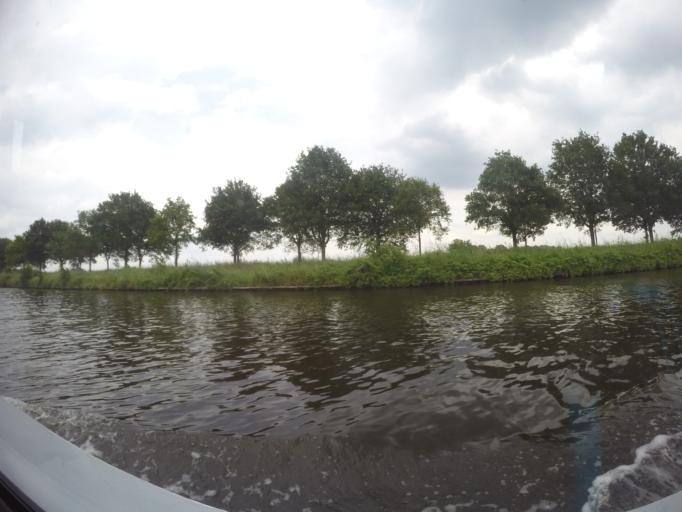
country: NL
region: Overijssel
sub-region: Gemeente Hof van Twente
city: Delden
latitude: 52.2673
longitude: 6.6446
